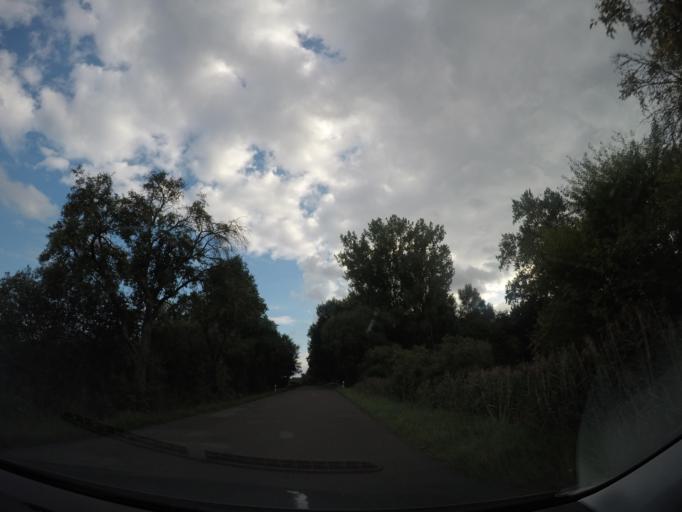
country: DE
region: Saxony-Anhalt
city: Mieste
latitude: 52.4798
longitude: 11.1360
